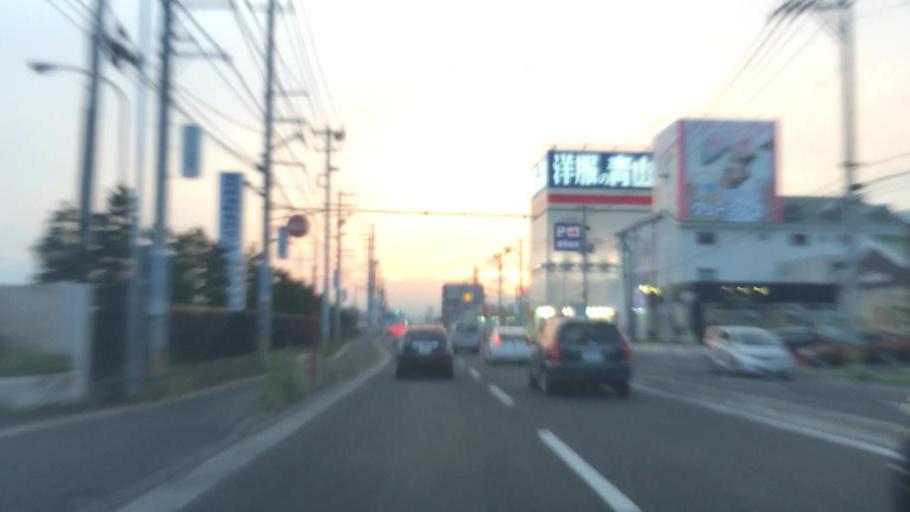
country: JP
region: Miyagi
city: Sendai-shi
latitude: 38.3142
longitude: 140.9057
